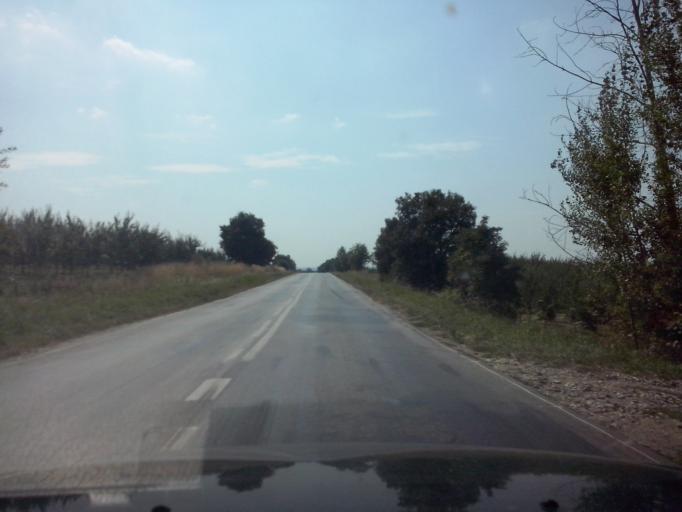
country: PL
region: Swietokrzyskie
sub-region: Powiat staszowski
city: Szydlow
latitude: 50.6044
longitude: 21.0094
